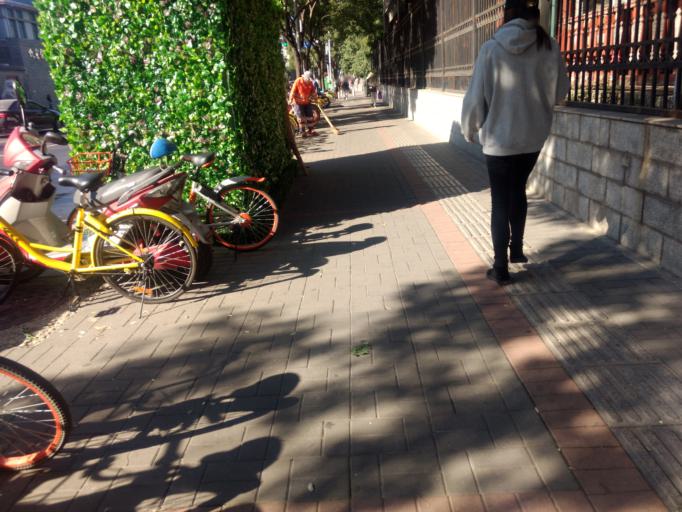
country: CN
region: Beijing
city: Beijing
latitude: 39.8951
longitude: 116.3784
